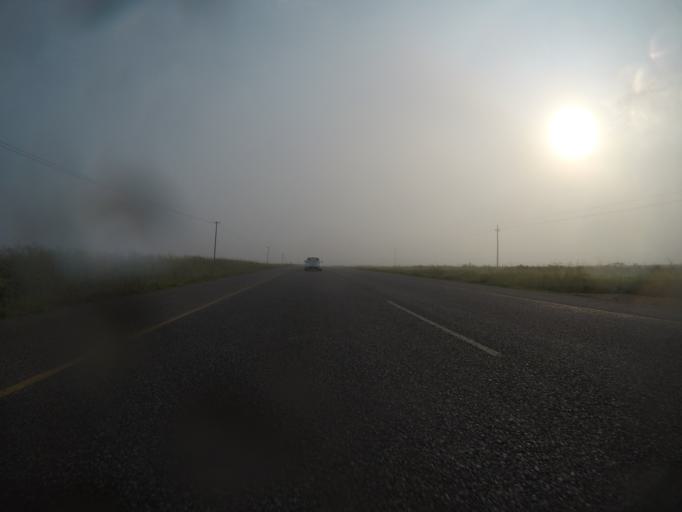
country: ZA
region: Western Cape
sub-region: West Coast District Municipality
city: Malmesbury
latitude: -33.6498
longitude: 18.7109
